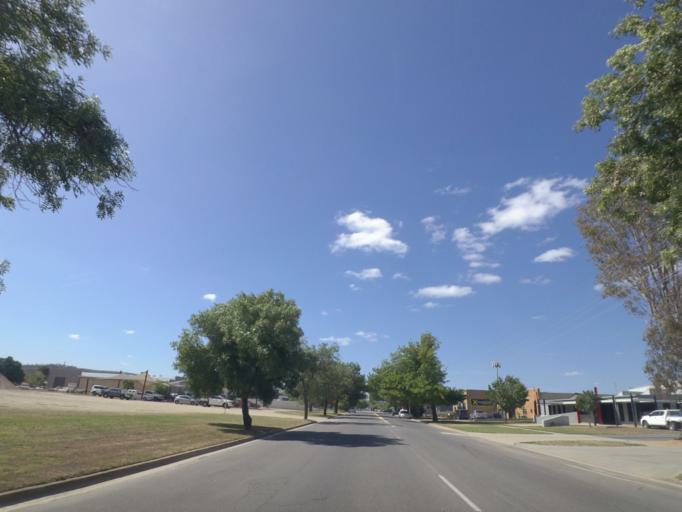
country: AU
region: New South Wales
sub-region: Albury Municipality
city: South Albury
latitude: -36.0924
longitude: 146.9134
